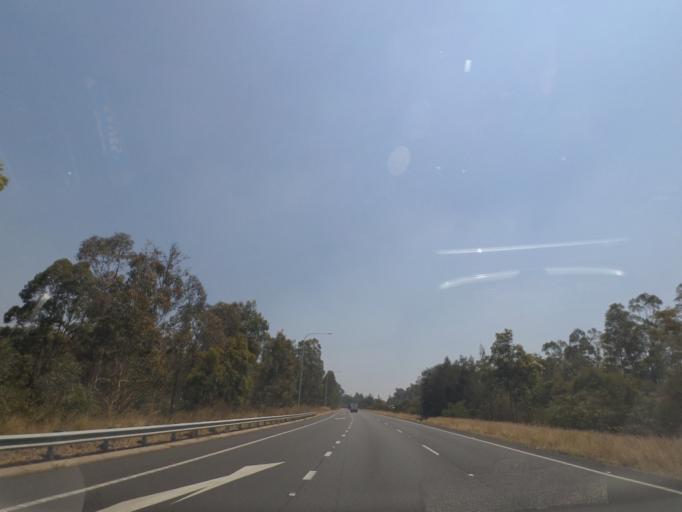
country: AU
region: New South Wales
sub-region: Newcastle
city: Beresfield
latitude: -32.8332
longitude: 151.6347
